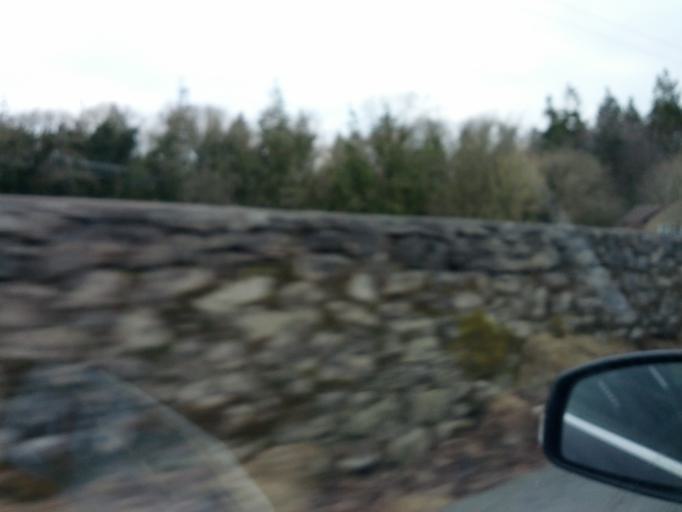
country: IE
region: Connaught
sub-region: County Galway
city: Oranmore
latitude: 53.2344
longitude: -8.8420
